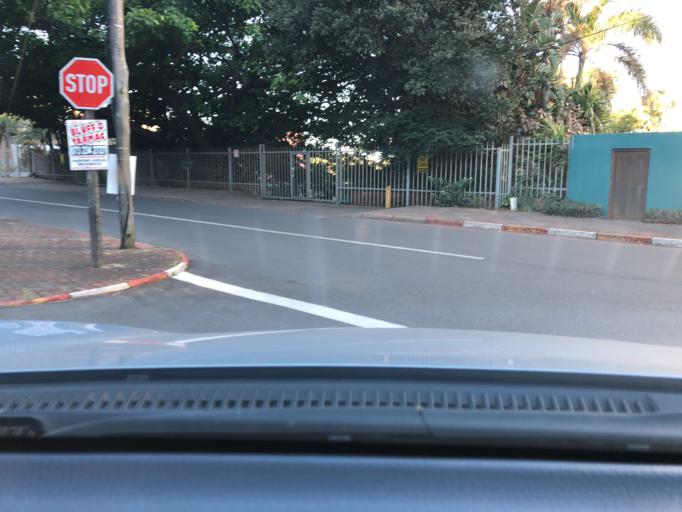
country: ZA
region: KwaZulu-Natal
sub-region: eThekwini Metropolitan Municipality
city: Umkomaas
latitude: -30.0441
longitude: 30.8935
